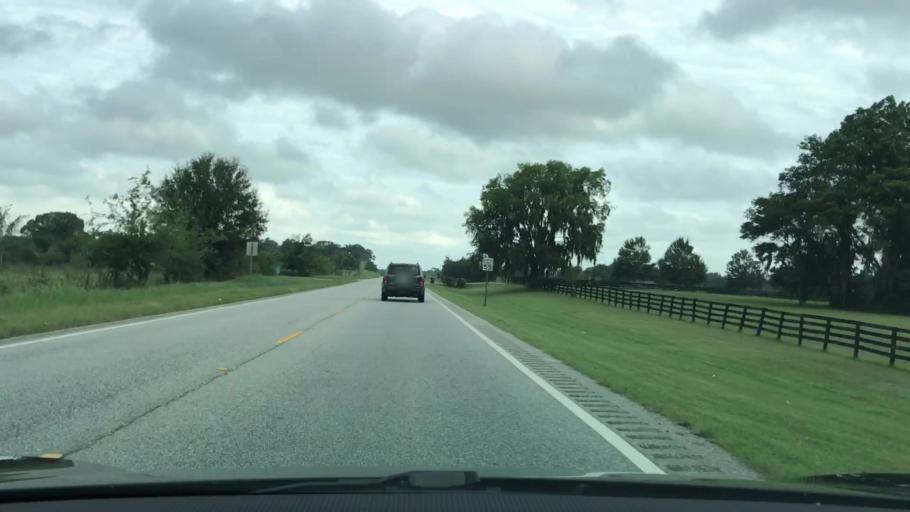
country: US
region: Alabama
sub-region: Montgomery County
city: Pike Road
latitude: 32.3281
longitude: -86.0527
